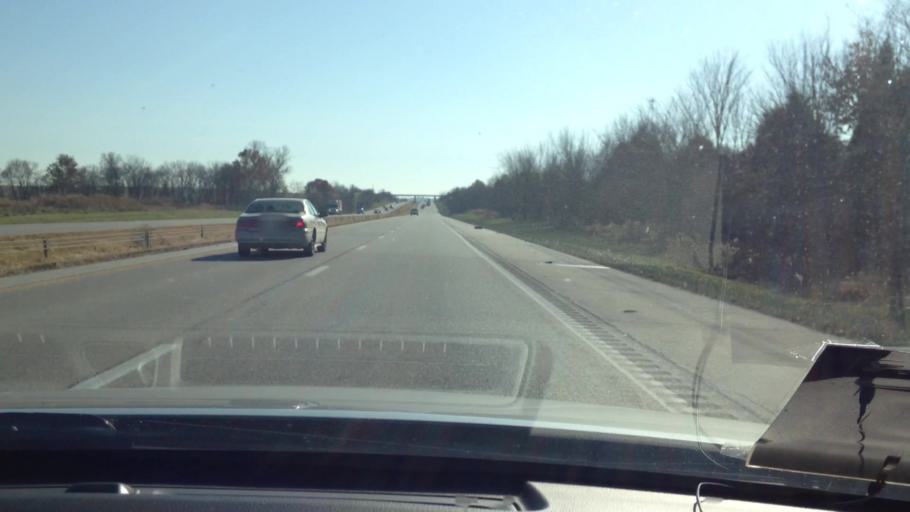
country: US
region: Missouri
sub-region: Platte County
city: Platte City
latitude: 39.4264
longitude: -94.7899
